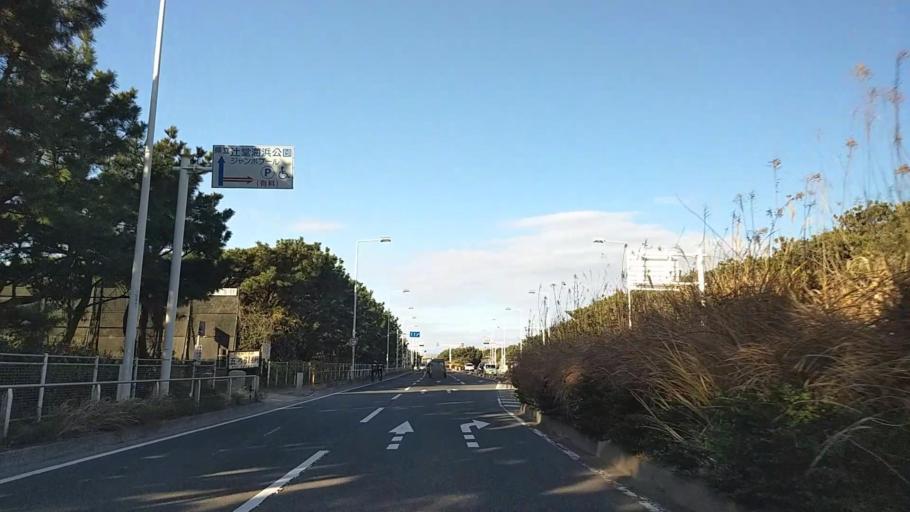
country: JP
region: Kanagawa
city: Fujisawa
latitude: 35.3190
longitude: 139.4525
